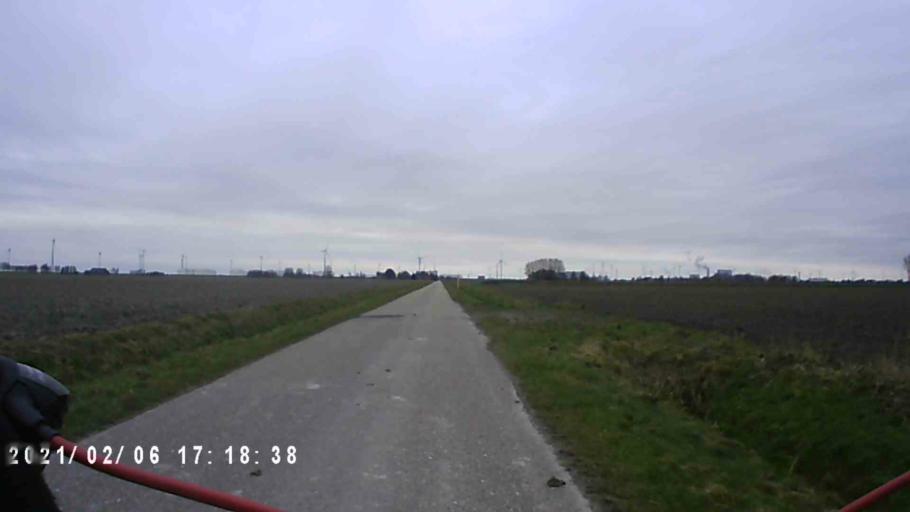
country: NL
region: Groningen
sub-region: Gemeente Appingedam
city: Appingedam
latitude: 53.4265
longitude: 6.7884
